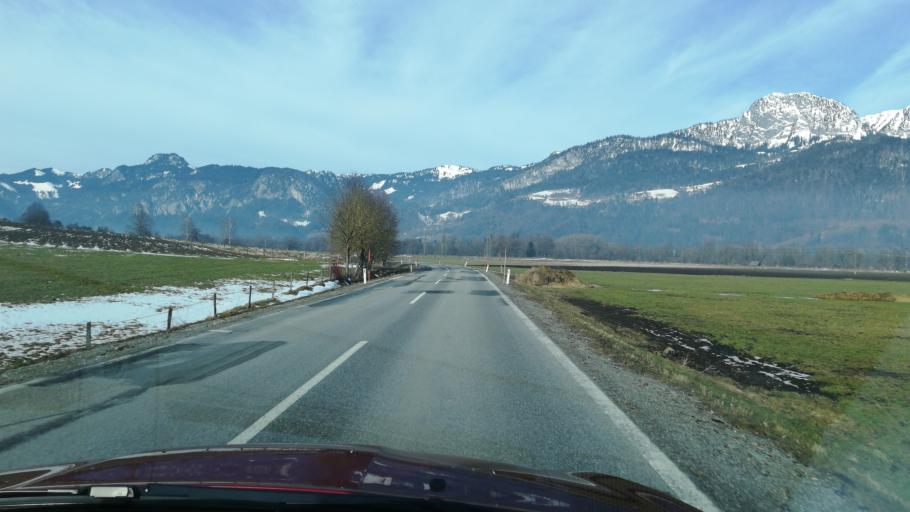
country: AT
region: Styria
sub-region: Politischer Bezirk Liezen
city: Weissenbach bei Liezen
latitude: 47.5458
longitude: 14.1985
